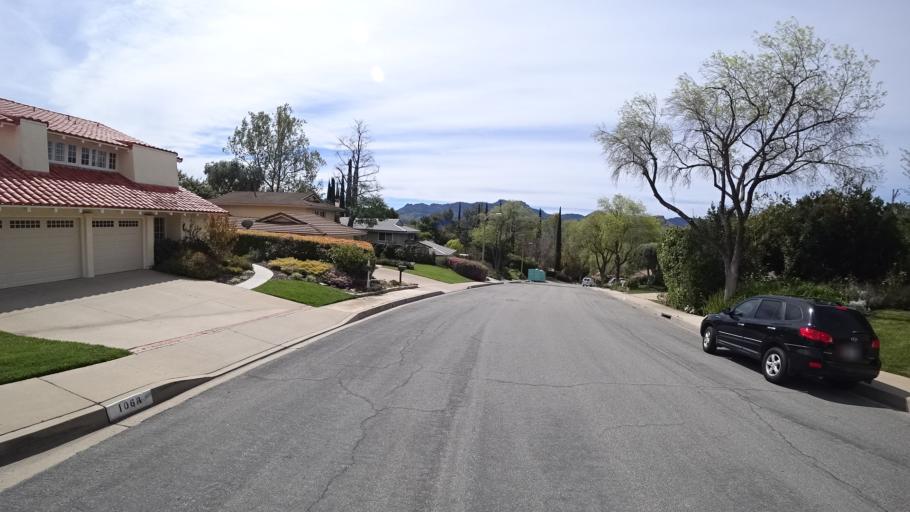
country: US
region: California
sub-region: Ventura County
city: Thousand Oaks
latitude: 34.1531
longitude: -118.8472
